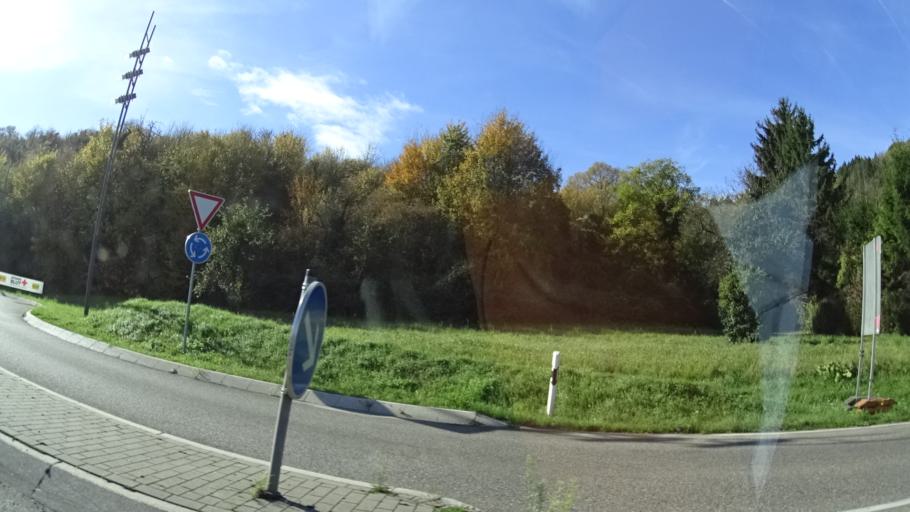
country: DE
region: Baden-Wuerttemberg
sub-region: Karlsruhe Region
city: Joehlingen
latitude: 48.9913
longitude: 8.5346
